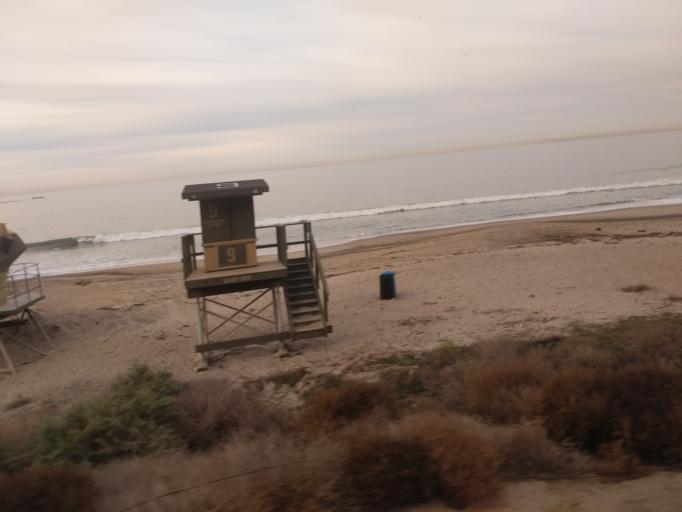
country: US
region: California
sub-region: Orange County
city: San Clemente
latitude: 33.4116
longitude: -117.6124
